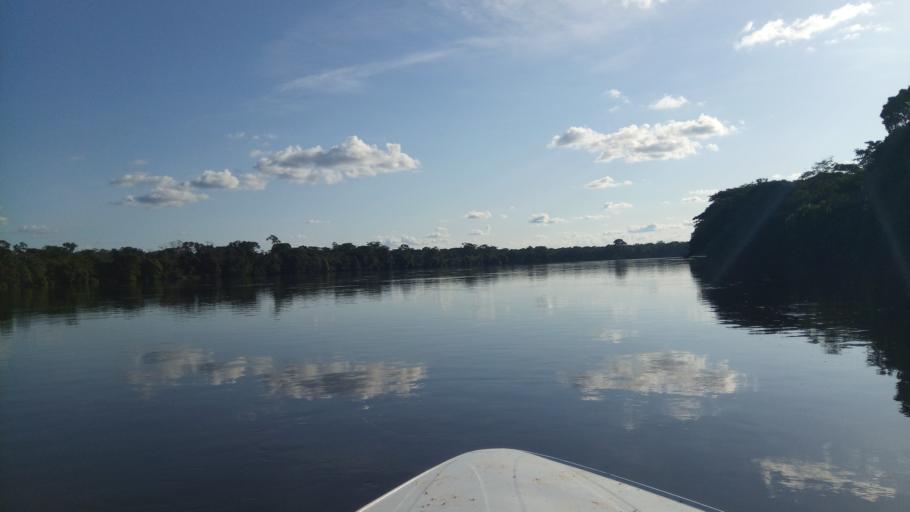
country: CD
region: Eastern Province
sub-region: Sous-Region de la Tshopo
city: Yangambi
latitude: 0.2349
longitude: 24.1062
